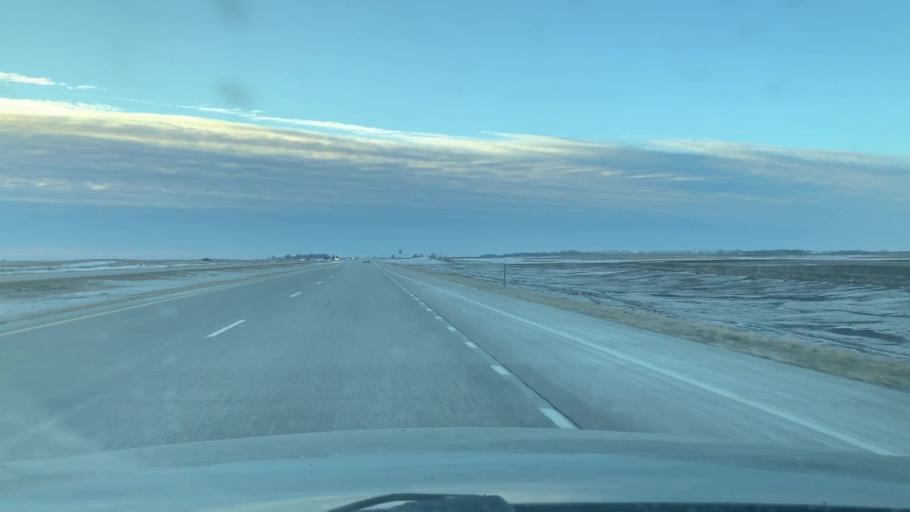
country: US
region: North Dakota
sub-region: Ransom County
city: Sheldon
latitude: 46.8759
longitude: -97.5004
